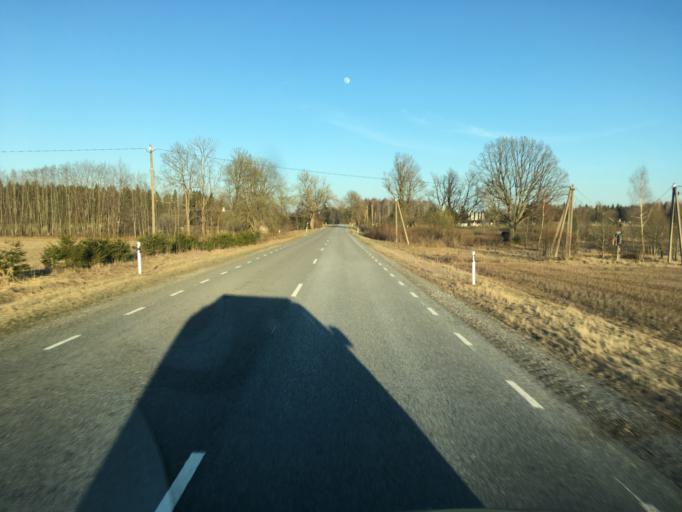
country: EE
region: Raplamaa
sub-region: Rapla vald
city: Rapla
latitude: 59.0769
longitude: 24.8666
